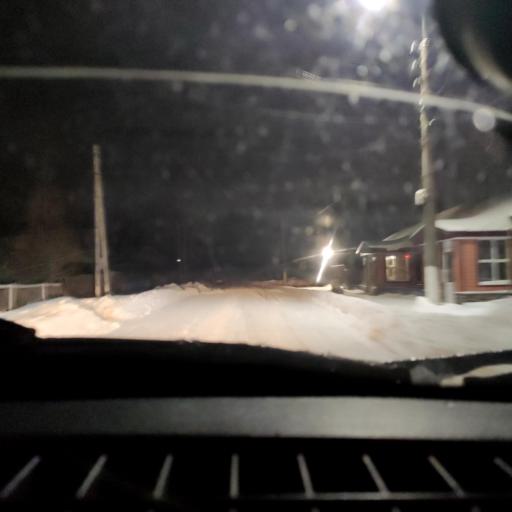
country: RU
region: Bashkortostan
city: Iglino
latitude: 54.8336
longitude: 56.4261
